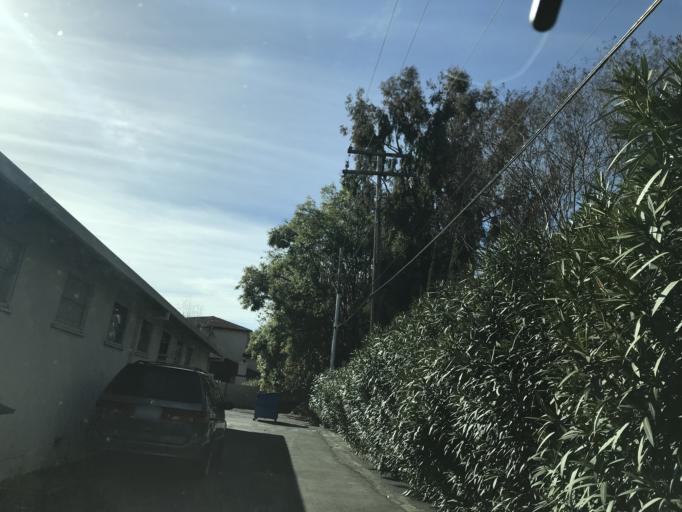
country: US
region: California
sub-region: Santa Clara County
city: Sunnyvale
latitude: 37.3727
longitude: -122.0596
